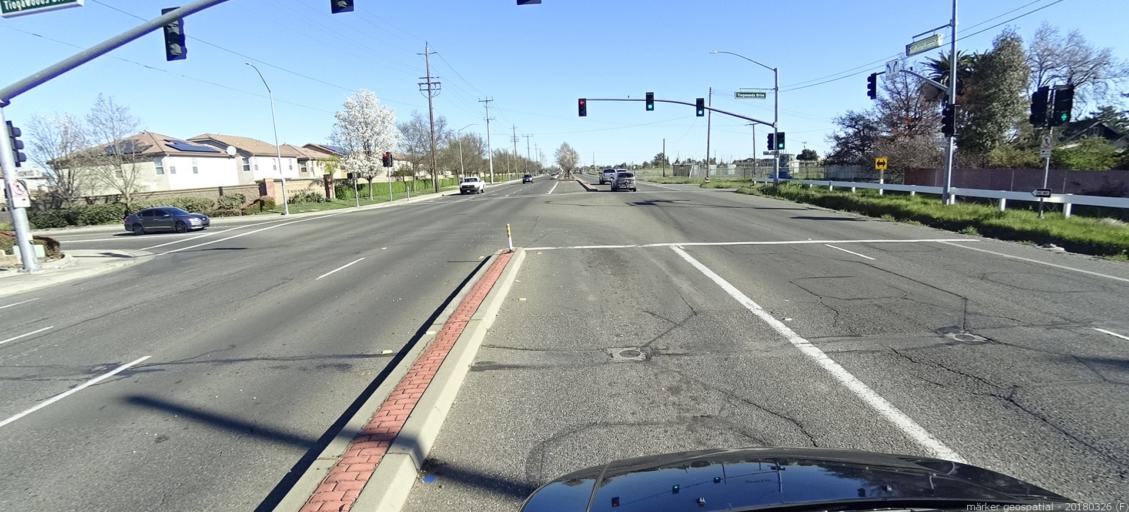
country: US
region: California
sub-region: Sacramento County
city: Vineyard
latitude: 38.4771
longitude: -121.3719
